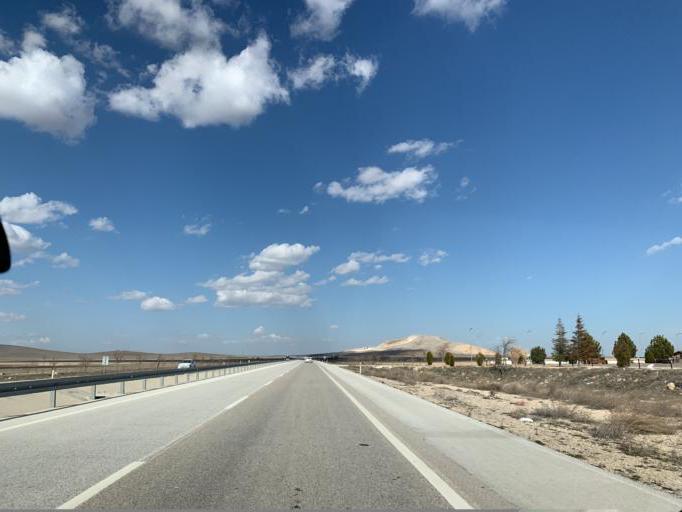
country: TR
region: Konya
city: Cihanbeyli
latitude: 38.5408
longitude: 32.8820
